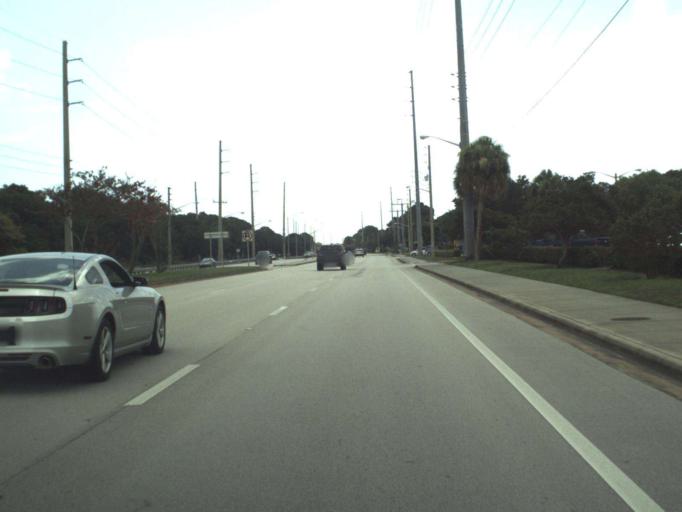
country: US
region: Florida
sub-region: Saint Lucie County
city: Fort Pierce South
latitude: 27.4254
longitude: -80.3574
